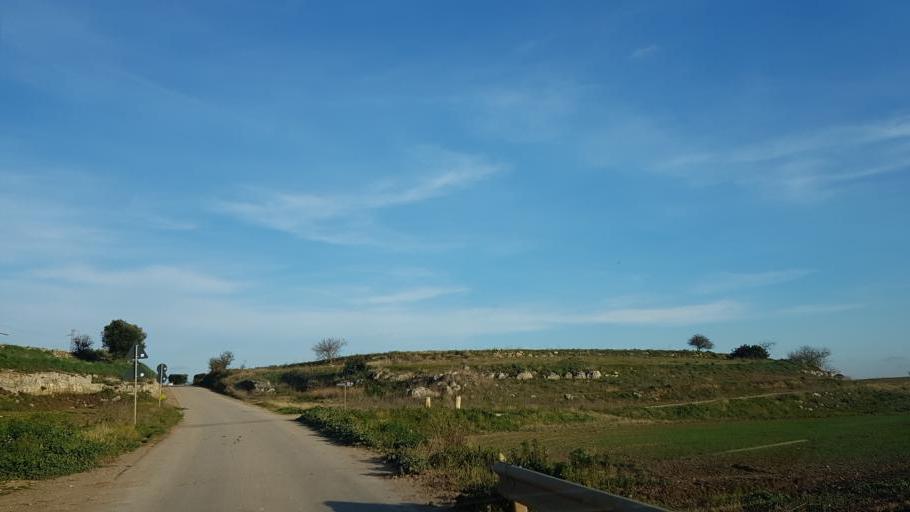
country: IT
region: Apulia
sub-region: Provincia di Brindisi
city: San Vito dei Normanni
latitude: 40.6648
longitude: 17.7967
